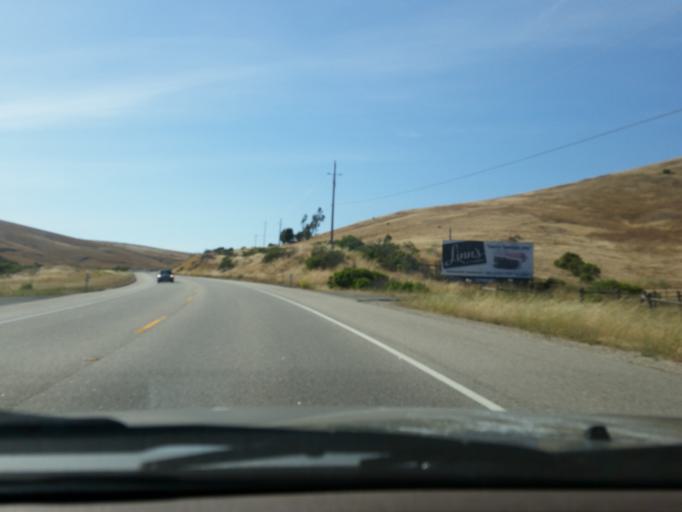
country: US
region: California
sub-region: San Luis Obispo County
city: Cayucos
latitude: 35.4780
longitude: -120.9915
